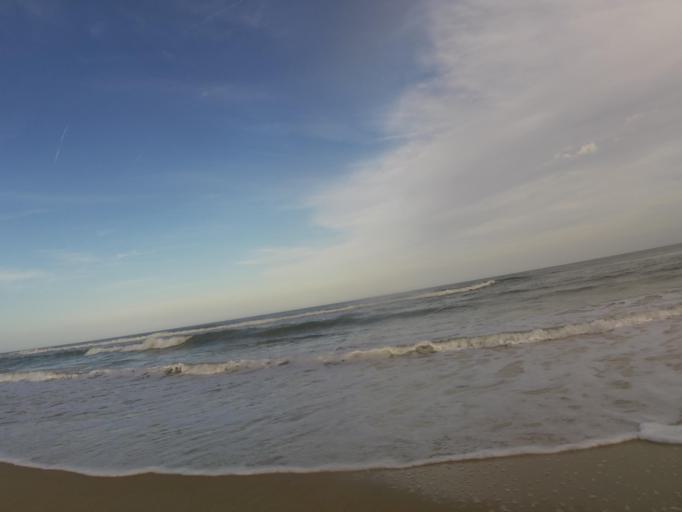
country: US
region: Florida
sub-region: Flagler County
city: Palm Coast
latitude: 29.6225
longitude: -81.1928
